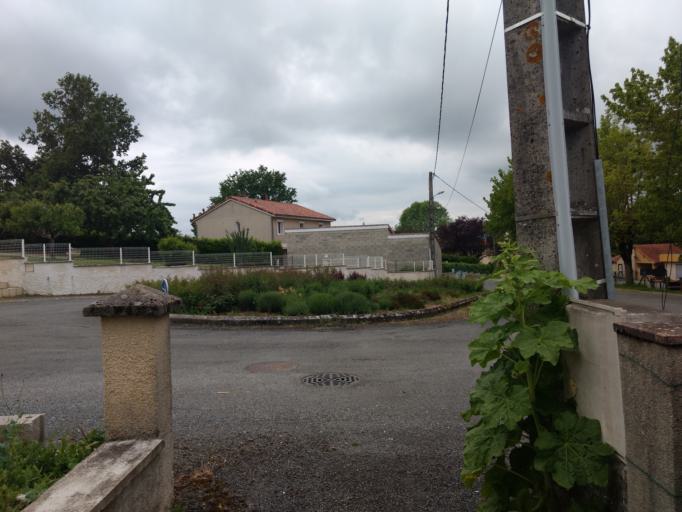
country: FR
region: Midi-Pyrenees
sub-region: Departement de l'Aveyron
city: Capdenac-Gare
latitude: 44.5375
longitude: 2.1076
